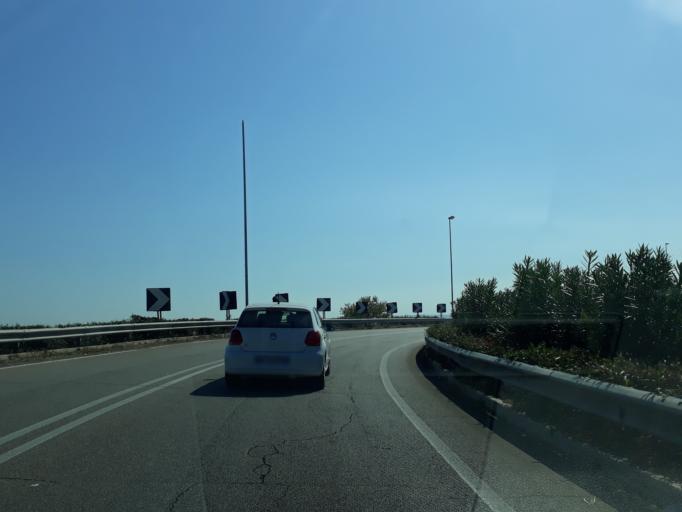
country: IT
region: Apulia
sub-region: Provincia di Bari
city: Monopoli
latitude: 40.9239
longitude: 17.3170
